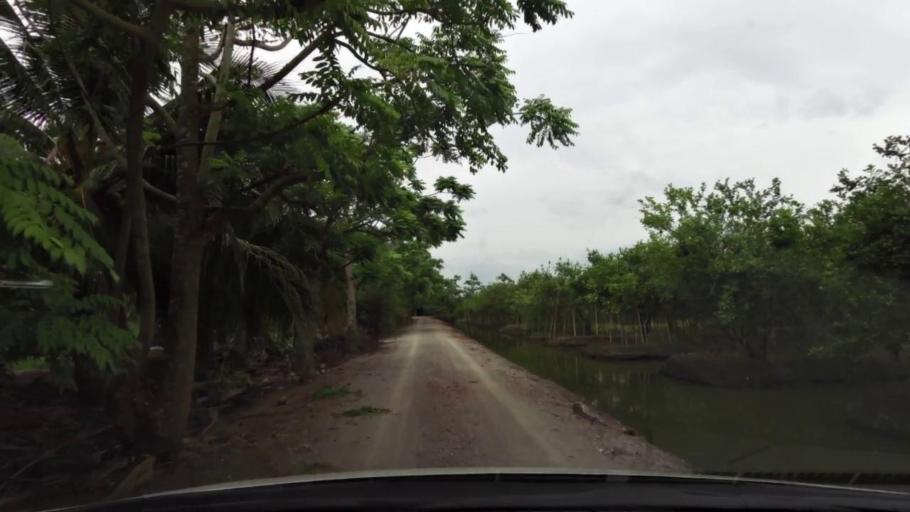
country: TH
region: Ratchaburi
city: Damnoen Saduak
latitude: 13.5575
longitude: 100.0079
